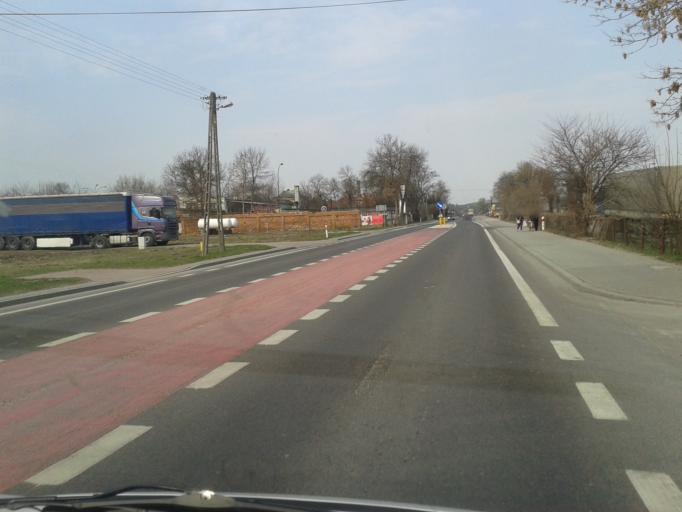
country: PL
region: Lublin Voivodeship
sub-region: Powiat tomaszowski
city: Belzec
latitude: 50.3757
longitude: 23.4502
